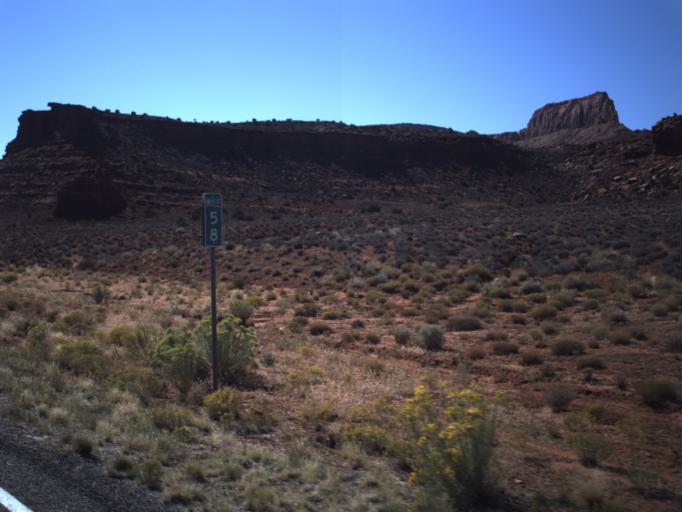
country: US
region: Utah
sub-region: San Juan County
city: Blanding
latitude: 37.7822
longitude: -110.2928
